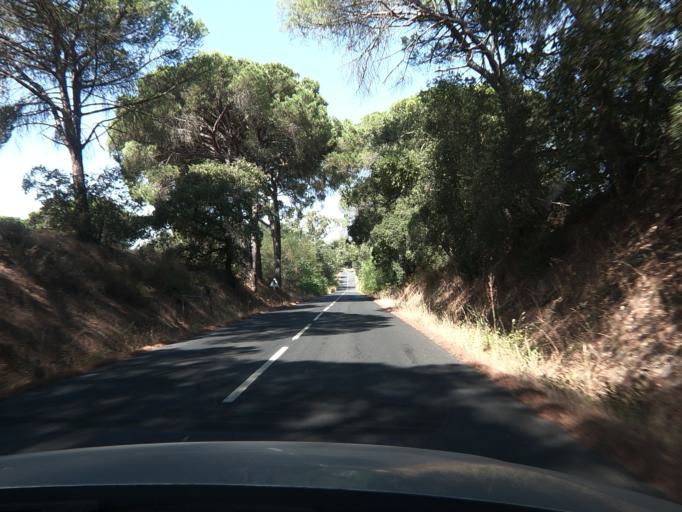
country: PT
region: Setubal
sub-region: Alcacer do Sal
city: Alcacer do Sal
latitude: 38.3531
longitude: -8.4700
